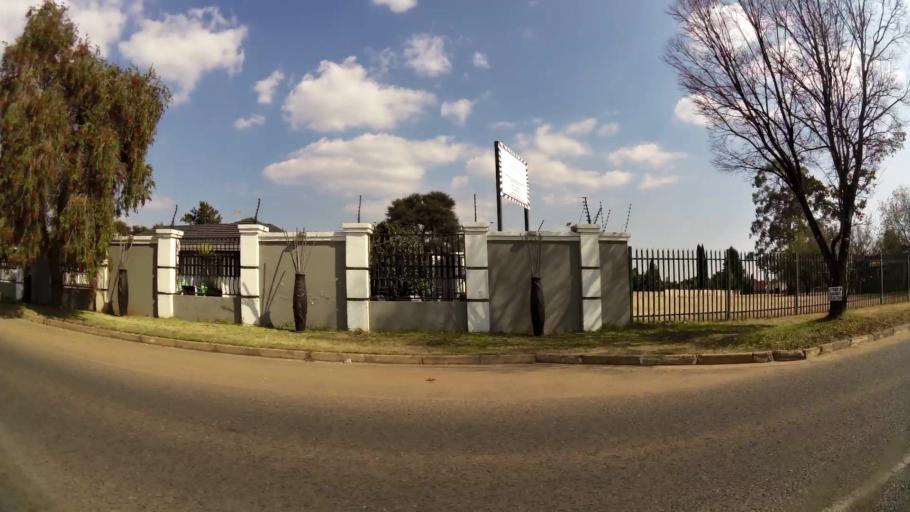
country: ZA
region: Gauteng
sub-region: City of Johannesburg Metropolitan Municipality
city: Modderfontein
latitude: -26.0949
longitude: 28.2508
